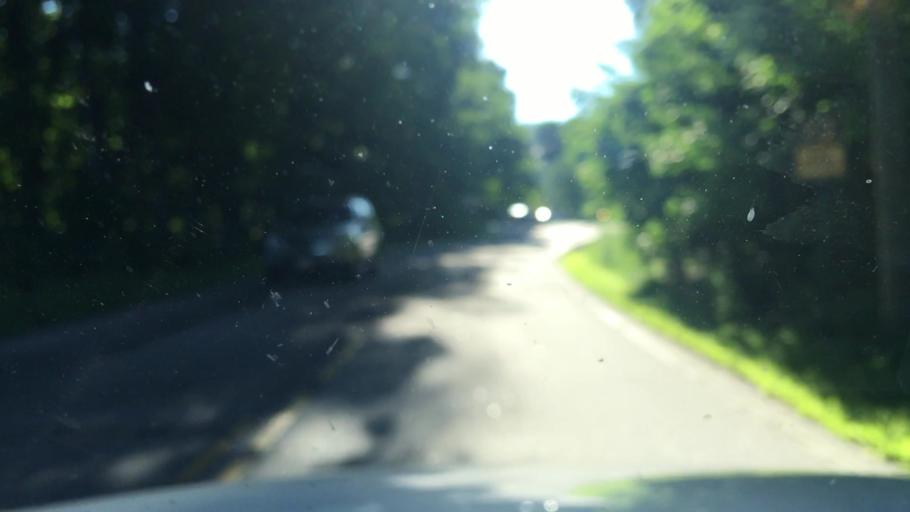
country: US
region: New Hampshire
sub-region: Rockingham County
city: Danville
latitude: 42.9060
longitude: -71.1546
